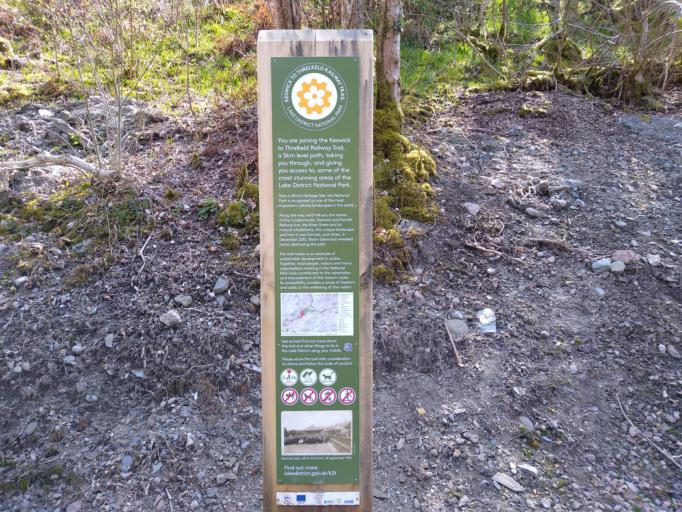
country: GB
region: England
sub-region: Cumbria
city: Keswick
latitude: 54.6069
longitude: -3.1074
